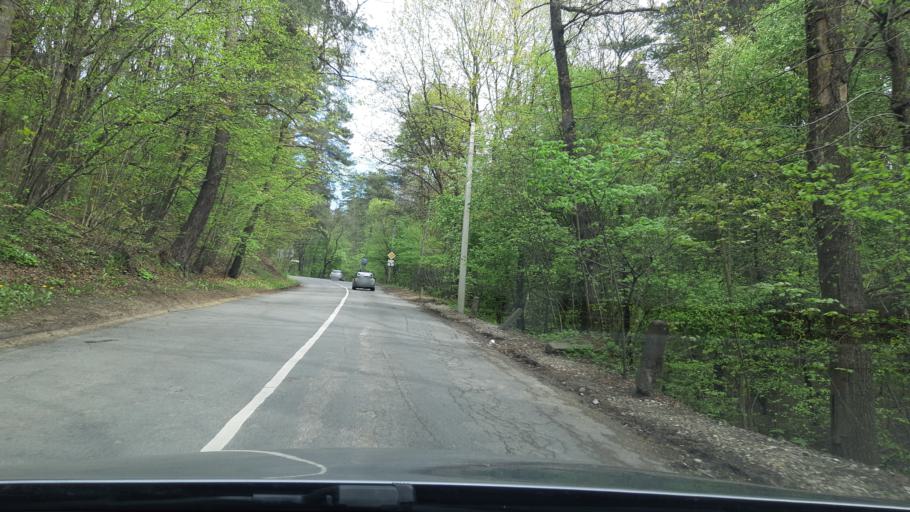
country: LT
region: Kauno apskritis
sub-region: Kauno rajonas
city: Akademija (Kaunas)
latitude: 54.9235
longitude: 23.8290
